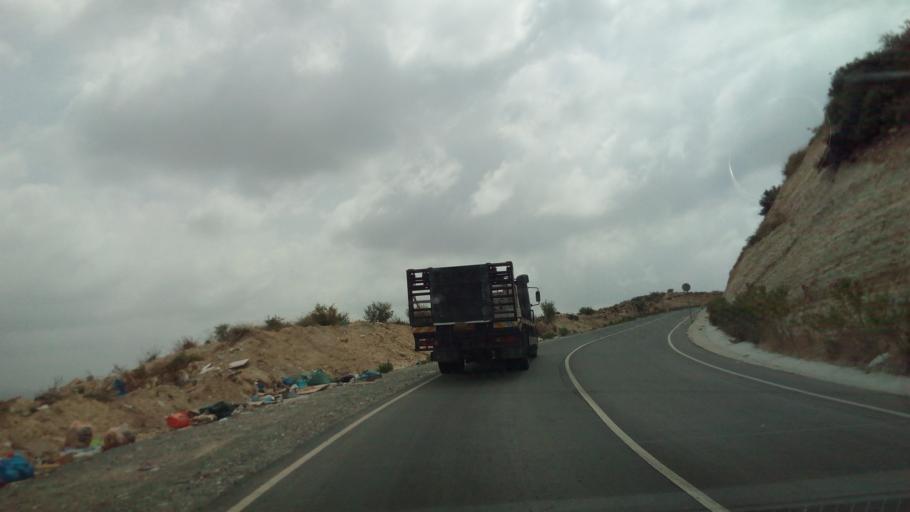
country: CY
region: Limassol
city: Ypsonas
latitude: 34.7483
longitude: 32.9478
